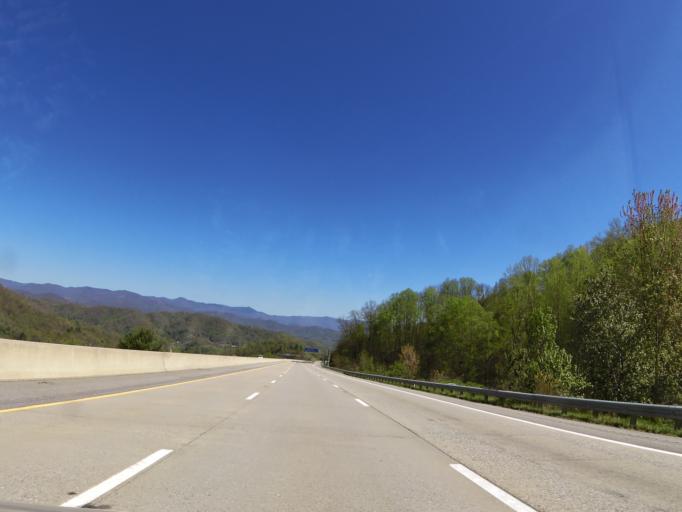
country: US
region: North Carolina
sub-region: Madison County
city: Mars Hill
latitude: 35.8786
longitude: -82.5484
